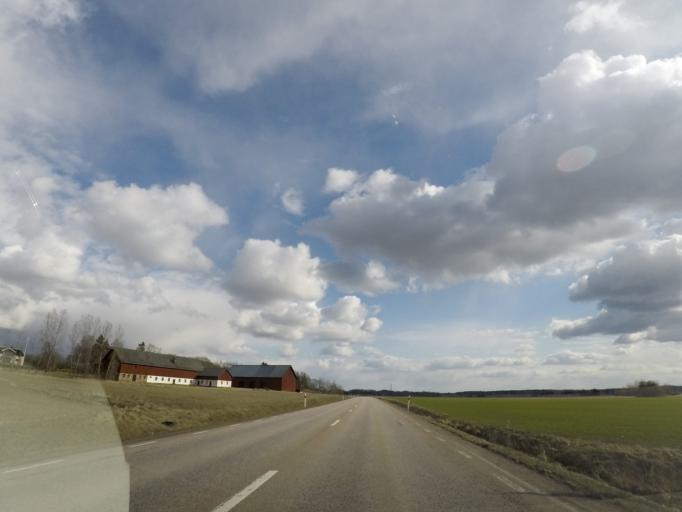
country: SE
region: Vaestmanland
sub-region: Hallstahammars Kommun
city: Hallstahammar
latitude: 59.5999
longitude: 16.2061
